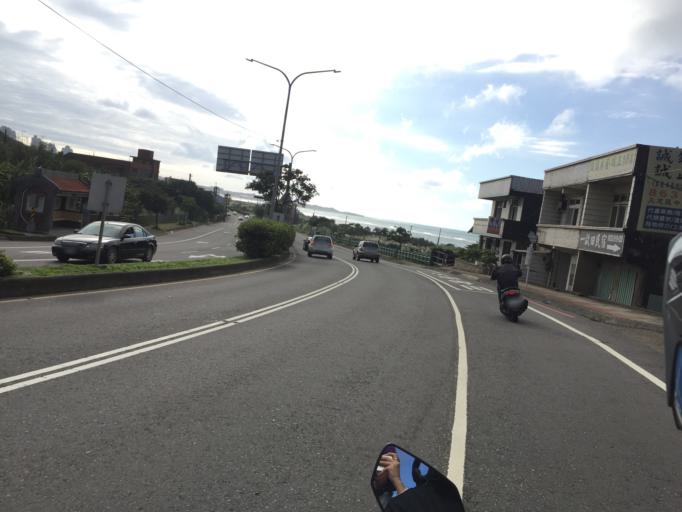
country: TW
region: Taipei
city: Taipei
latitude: 25.2638
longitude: 121.4819
